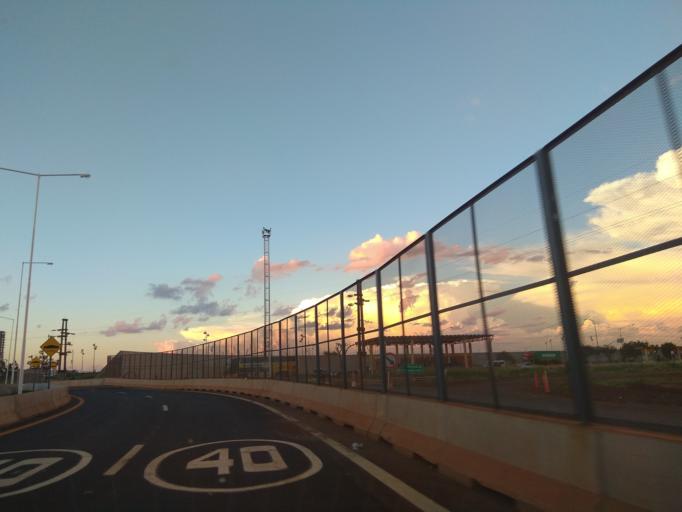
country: AR
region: Misiones
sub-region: Departamento de Capital
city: Posadas
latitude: -27.3766
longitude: -55.8842
